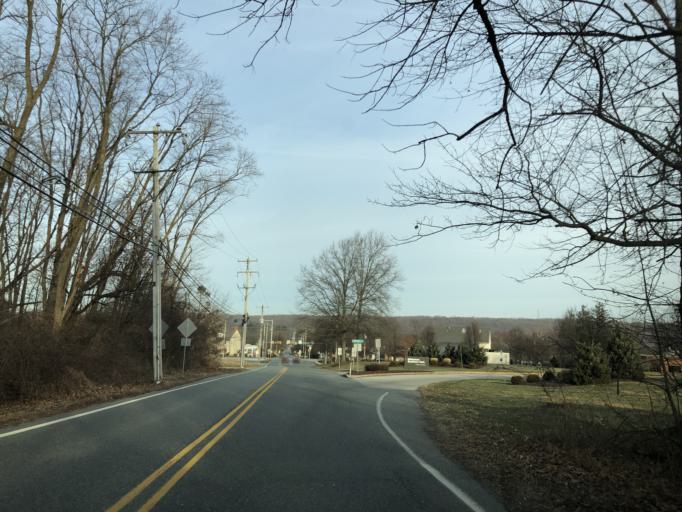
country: US
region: Pennsylvania
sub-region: Chester County
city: Exton
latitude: 40.0282
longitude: -75.6084
